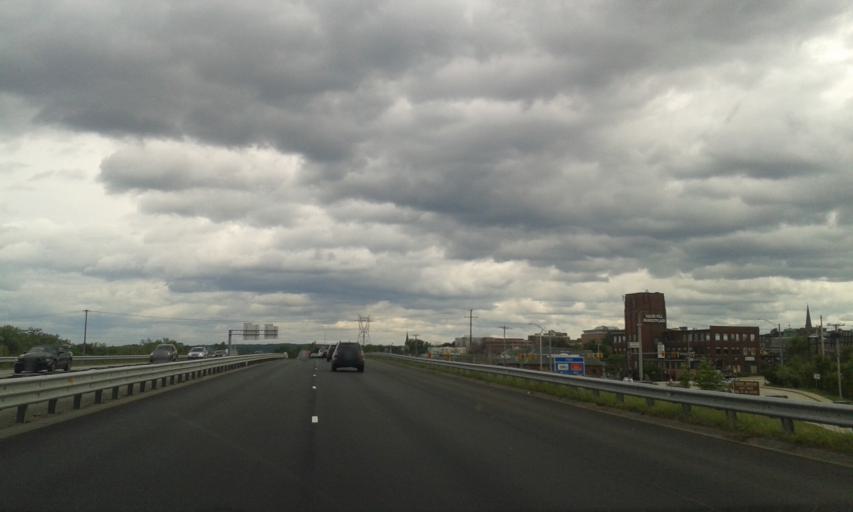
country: US
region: New Hampshire
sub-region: Merrimack County
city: Concord
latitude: 43.2108
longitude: -71.5337
